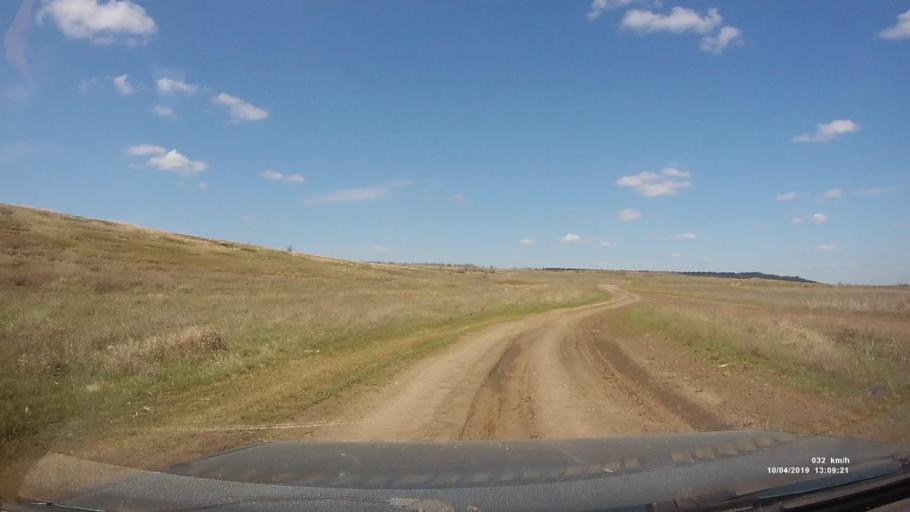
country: RU
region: Rostov
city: Masalovka
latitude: 48.4056
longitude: 40.2437
